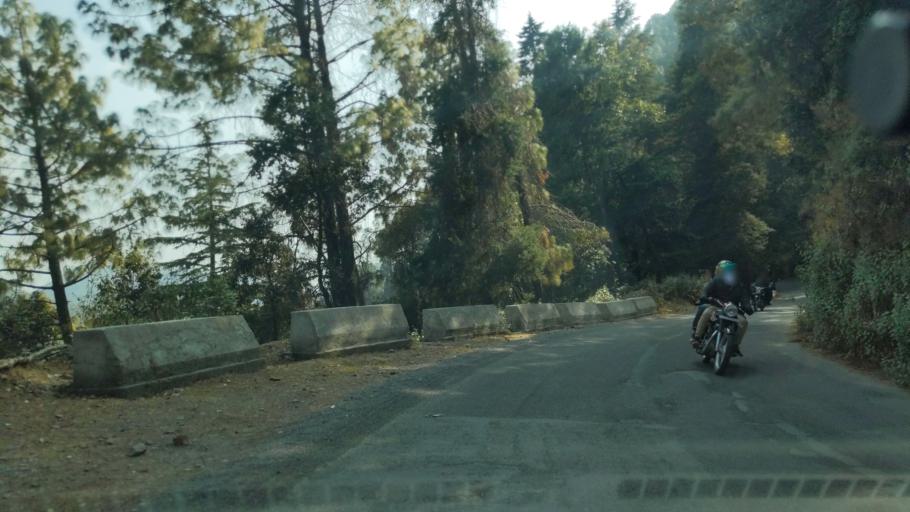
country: IN
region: Uttarakhand
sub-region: Naini Tal
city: Bhowali
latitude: 29.3974
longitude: 79.5381
